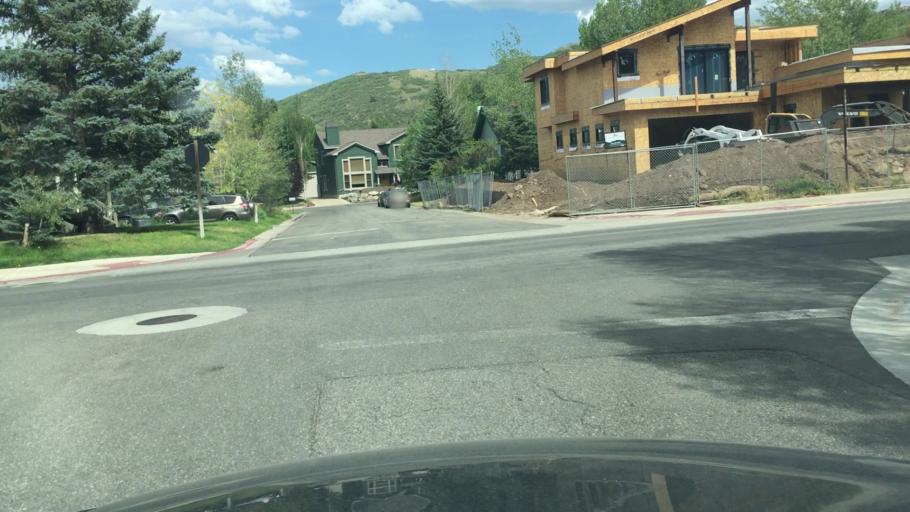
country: US
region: Utah
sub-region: Summit County
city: Park City
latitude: 40.6665
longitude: -111.4921
